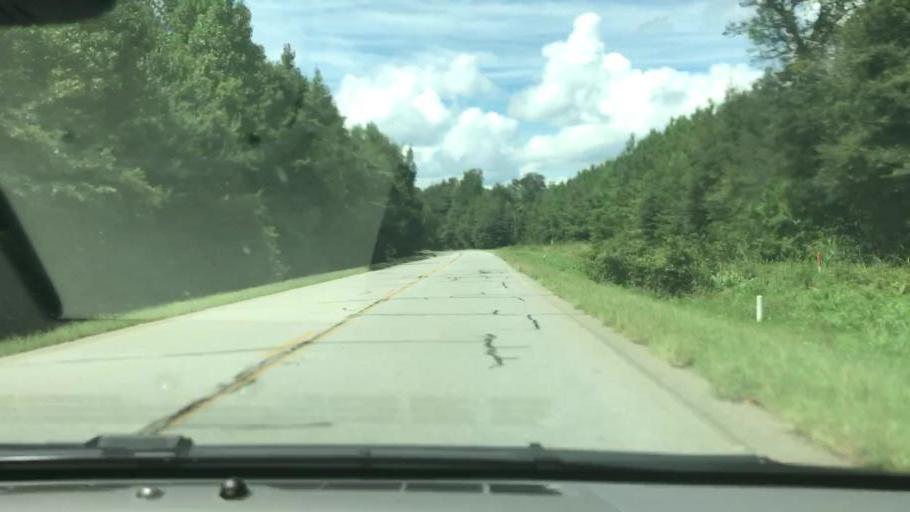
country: US
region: Georgia
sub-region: Stewart County
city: Lumpkin
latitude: 32.1453
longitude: -84.8874
